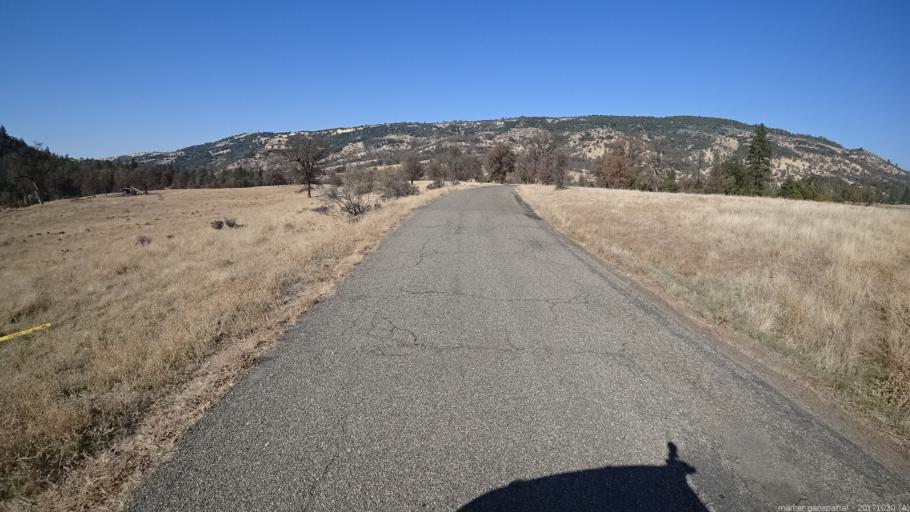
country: US
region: California
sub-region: Shasta County
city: Shingletown
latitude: 40.5488
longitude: -121.9114
